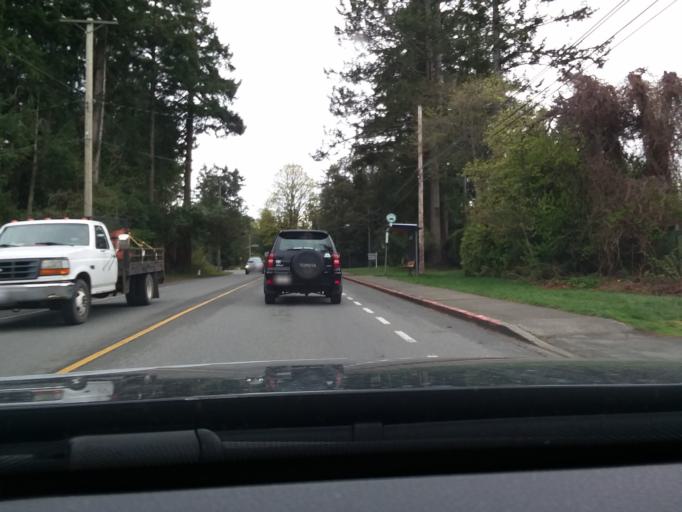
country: CA
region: British Columbia
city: North Saanich
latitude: 48.6183
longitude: -123.4165
